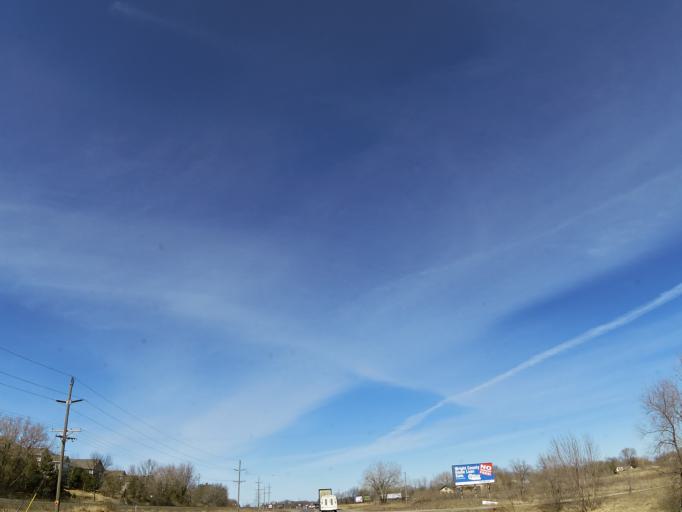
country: US
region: Minnesota
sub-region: Wright County
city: Buffalo
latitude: 45.1879
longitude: -93.8841
